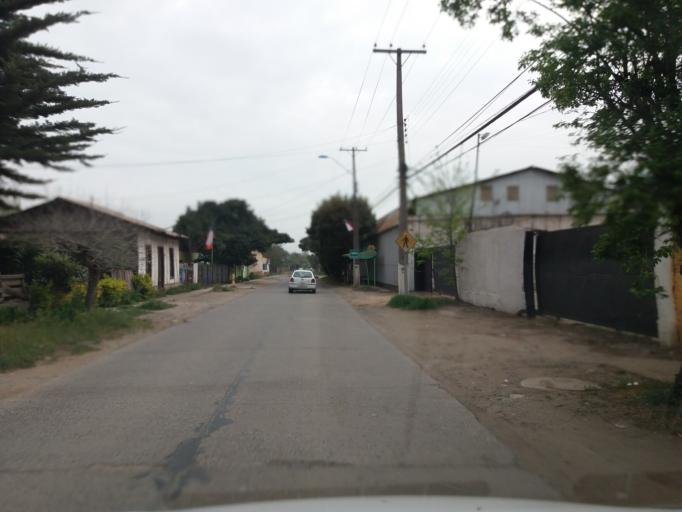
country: CL
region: Valparaiso
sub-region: Provincia de Quillota
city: Hacienda La Calera
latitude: -32.8239
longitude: -71.1297
